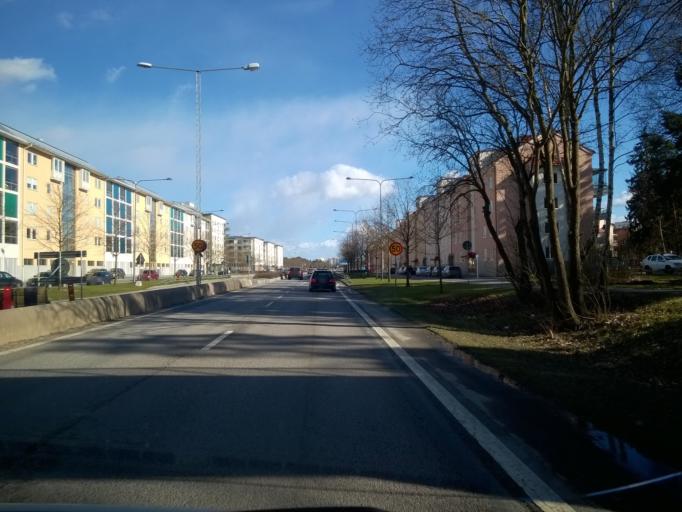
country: SE
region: Stockholm
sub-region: Jarfalla Kommun
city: Jakobsberg
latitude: 59.3729
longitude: 17.8426
